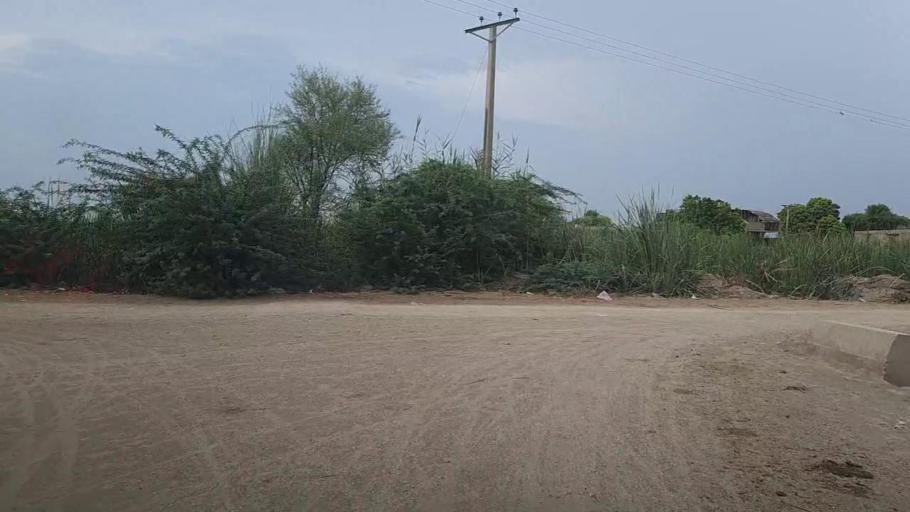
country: PK
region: Sindh
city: Karaundi
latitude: 26.9838
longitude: 68.4340
